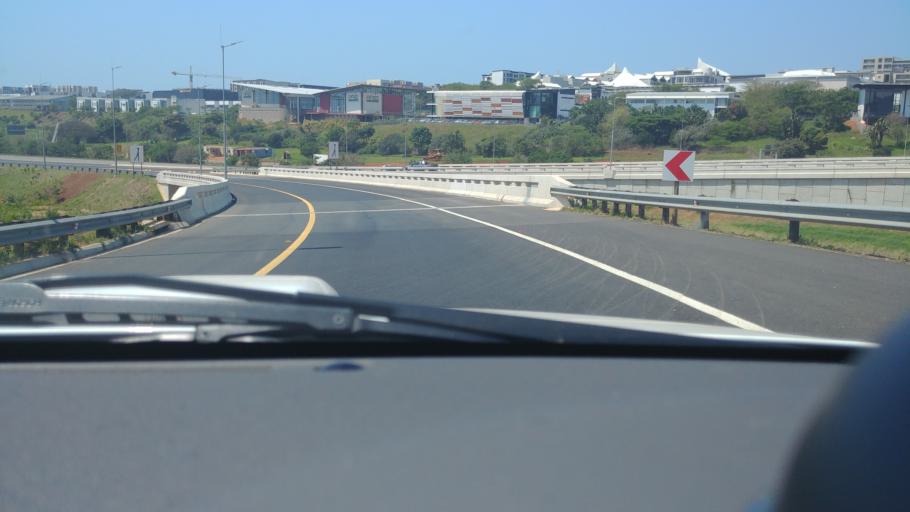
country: ZA
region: KwaZulu-Natal
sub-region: eThekwini Metropolitan Municipality
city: Durban
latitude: -29.7198
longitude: 31.0588
